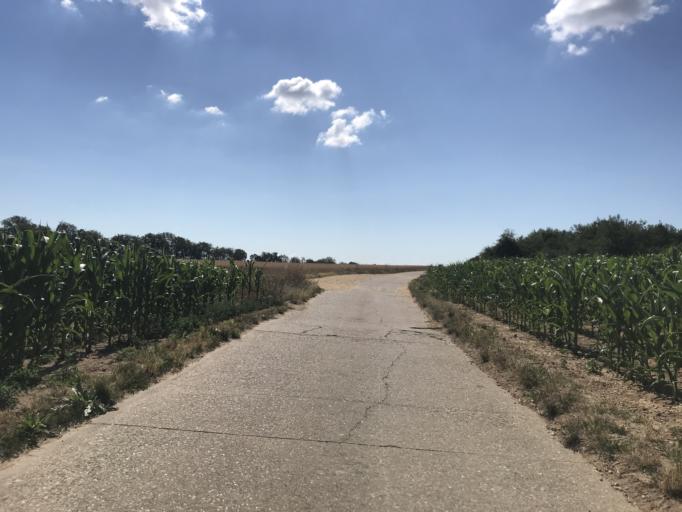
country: DE
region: Rheinland-Pfalz
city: Aspisheim
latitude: 49.9202
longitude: 7.9928
